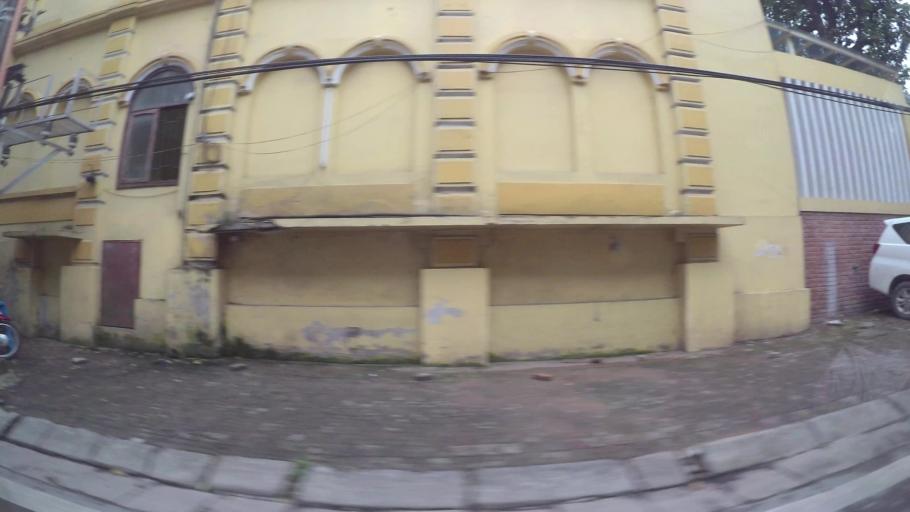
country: VN
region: Ha Noi
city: Hai BaTrung
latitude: 21.0177
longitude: 105.8591
